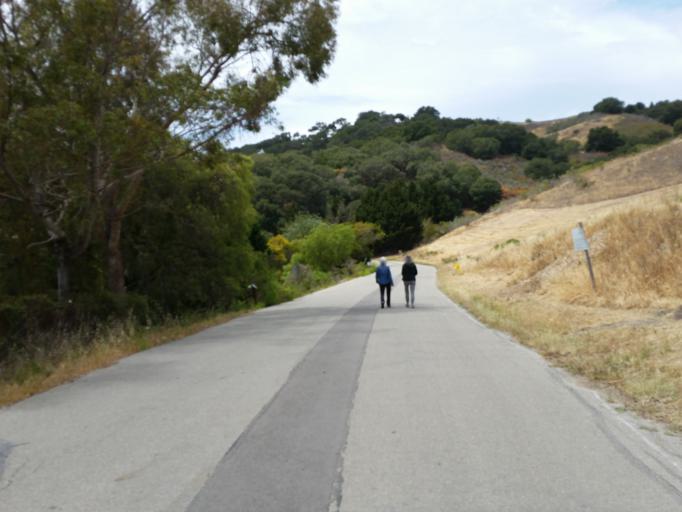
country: US
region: California
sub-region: San Luis Obispo County
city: Avila Beach
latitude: 35.1839
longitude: -120.7307
